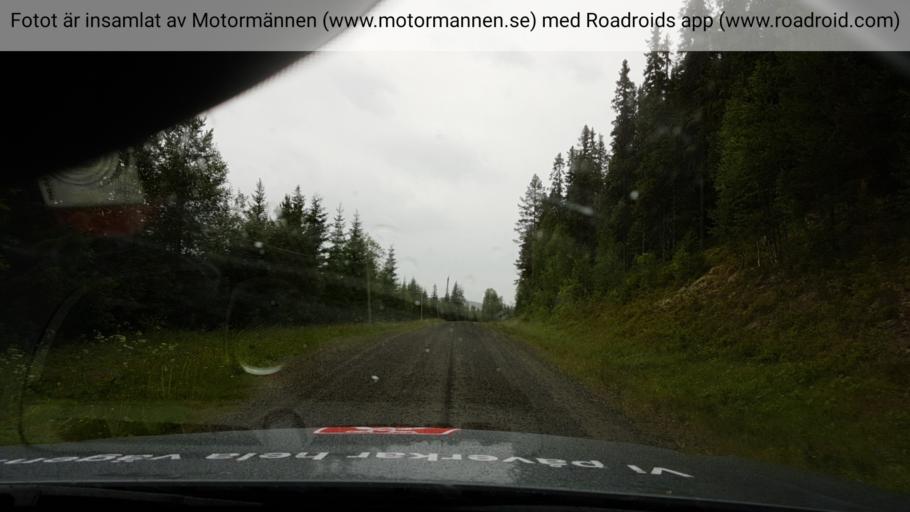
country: SE
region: Jaemtland
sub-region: Bergs Kommun
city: Hoverberg
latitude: 62.5560
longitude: 14.6898
